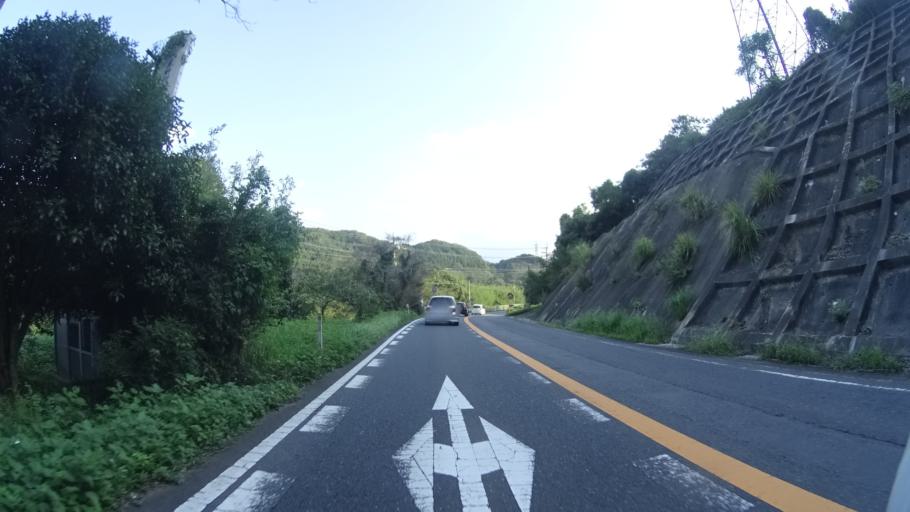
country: JP
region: Oita
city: Bungo-Takada-shi
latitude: 33.4817
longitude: 131.3348
